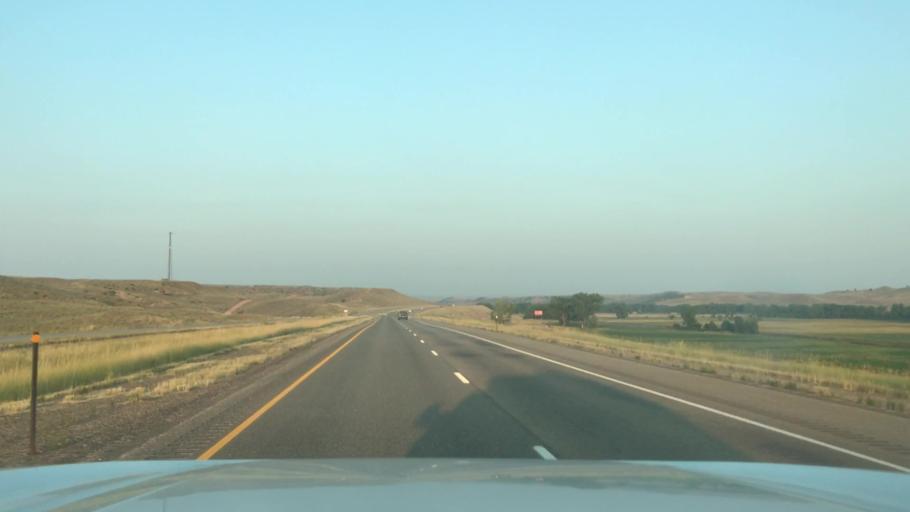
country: US
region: Wyoming
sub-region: Sheridan County
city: Sheridan
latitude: 44.9137
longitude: -107.0738
